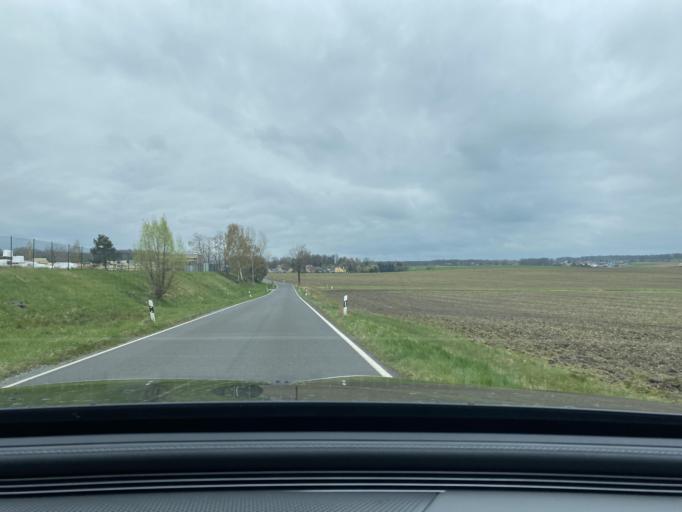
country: DE
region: Saxony
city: Puschwitz
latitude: 51.2554
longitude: 14.2985
